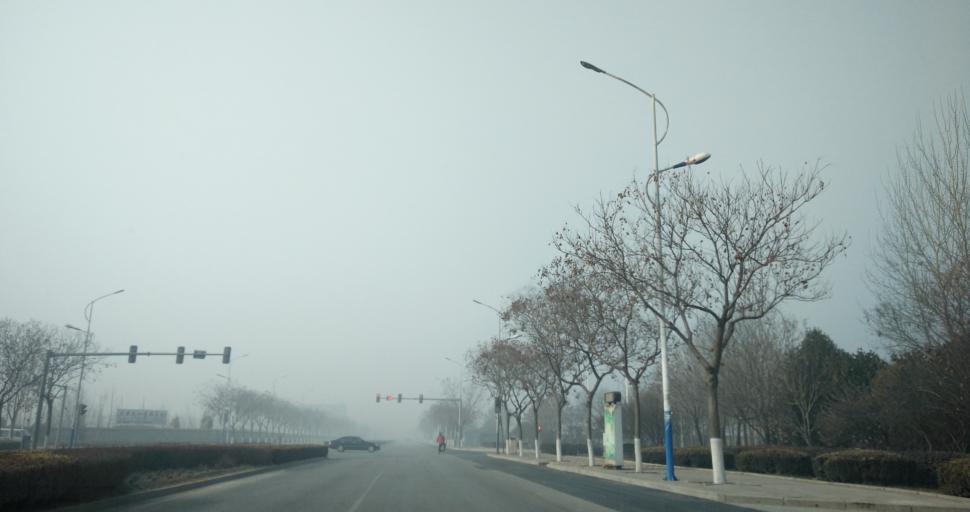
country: CN
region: Beijing
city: Yinghai
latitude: 39.7085
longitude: 116.4084
